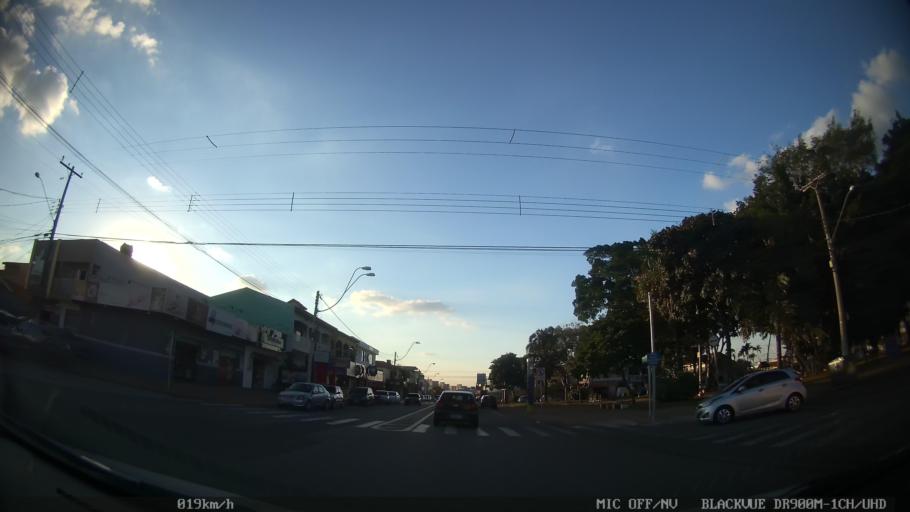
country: BR
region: Sao Paulo
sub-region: Americana
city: Americana
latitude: -22.7426
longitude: -47.3708
